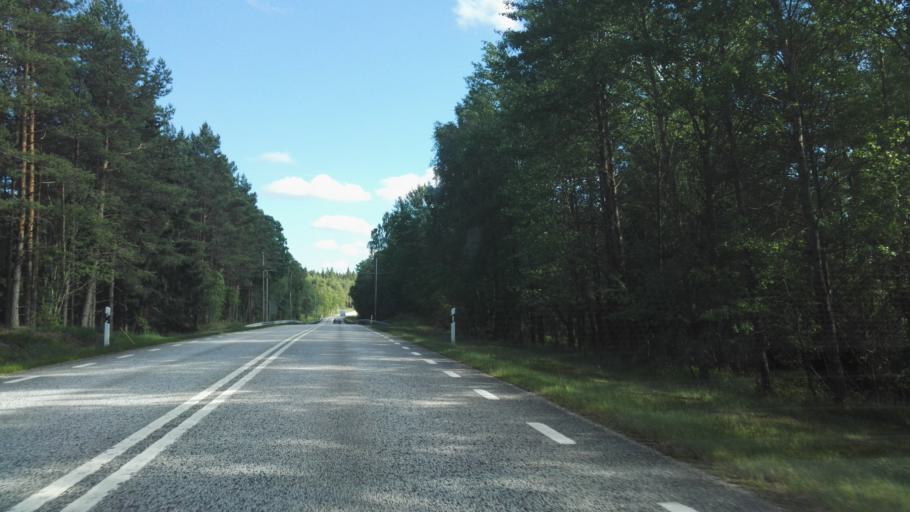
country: SE
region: Joenkoeping
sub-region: Savsjo Kommun
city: Stockaryd
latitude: 57.3042
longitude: 14.5181
